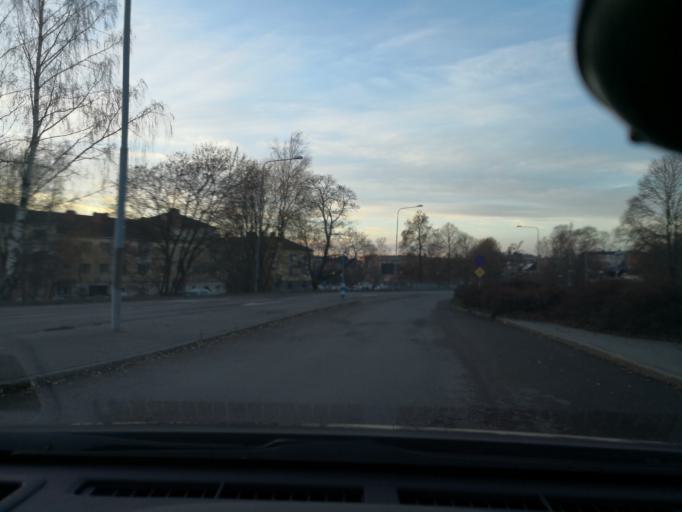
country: SE
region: Vaestmanland
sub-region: Kopings Kommun
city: Koping
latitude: 59.5140
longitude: 16.0014
